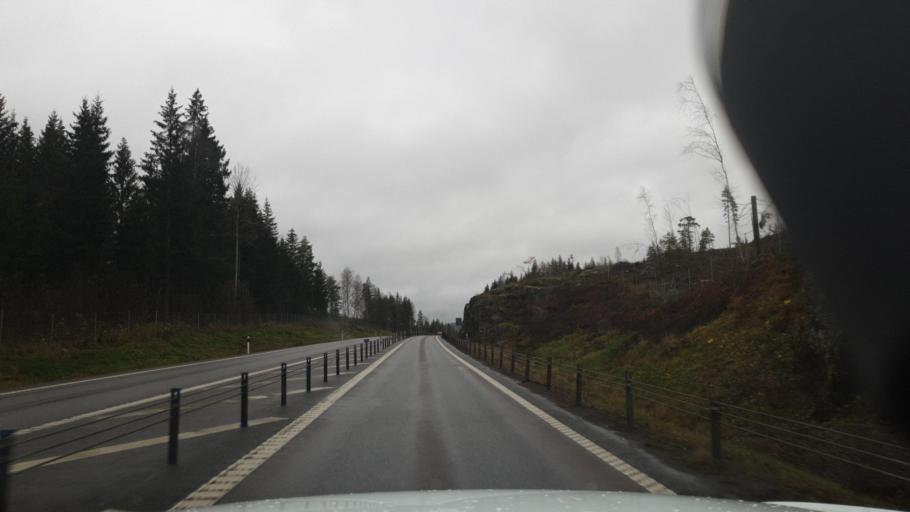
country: SE
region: Vaermland
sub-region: Arvika Kommun
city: Arvika
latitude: 59.6511
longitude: 12.7524
